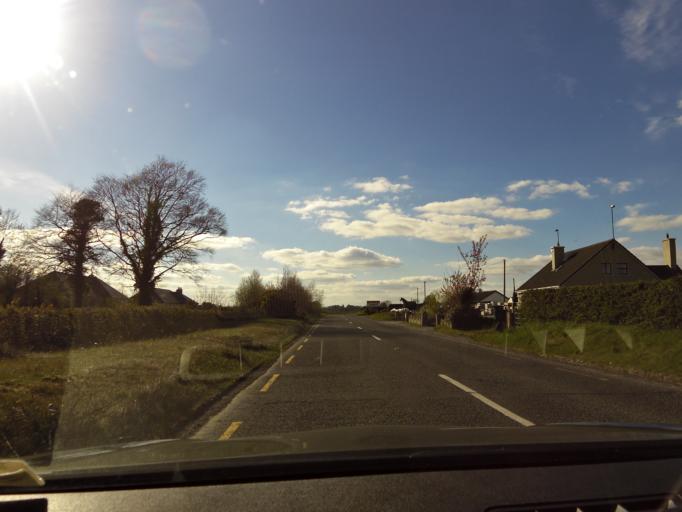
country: IE
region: Leinster
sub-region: Uibh Fhaili
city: Banagher
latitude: 53.1039
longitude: -8.0199
